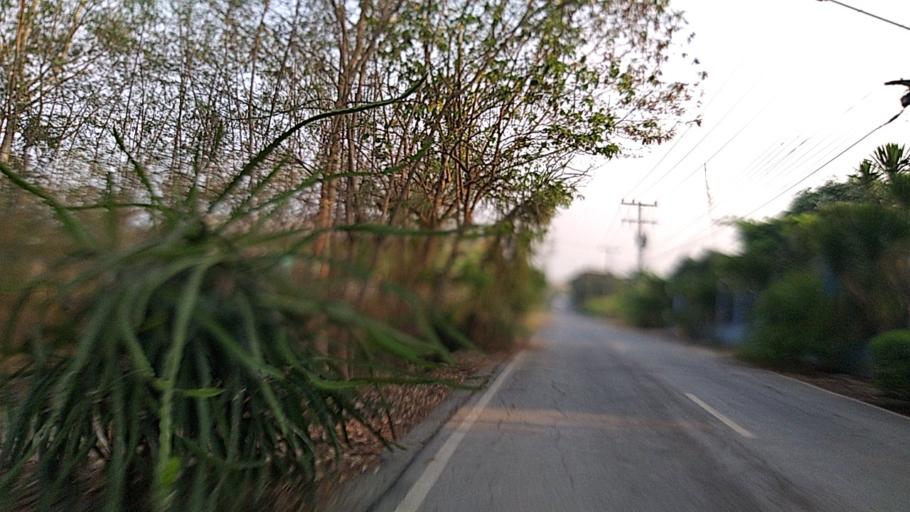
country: TH
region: Pathum Thani
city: Nong Suea
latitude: 14.0585
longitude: 100.8313
